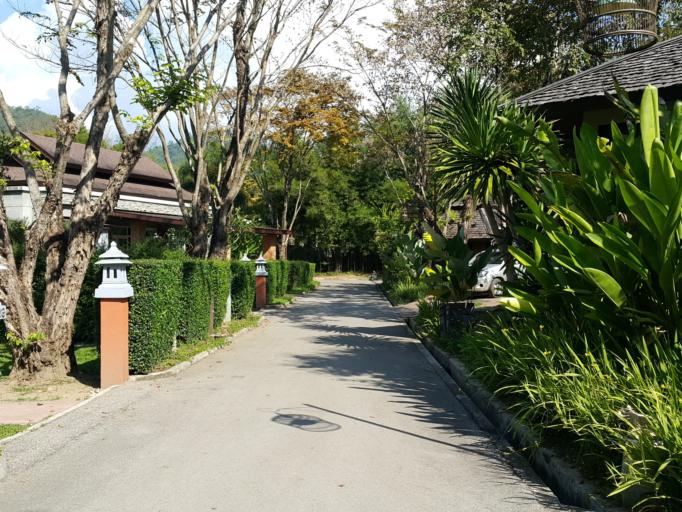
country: TH
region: Chiang Mai
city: Mae Taeng
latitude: 19.1993
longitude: 98.8856
